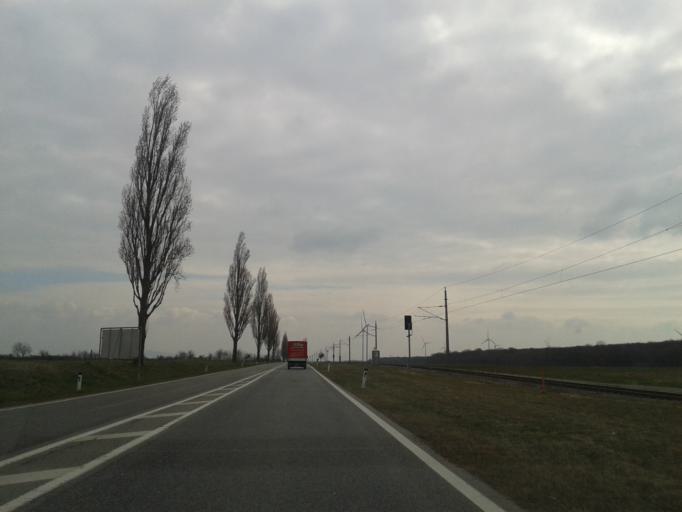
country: AT
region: Lower Austria
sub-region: Politischer Bezirk Ganserndorf
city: Orth an der Donau
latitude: 48.1097
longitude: 16.7129
